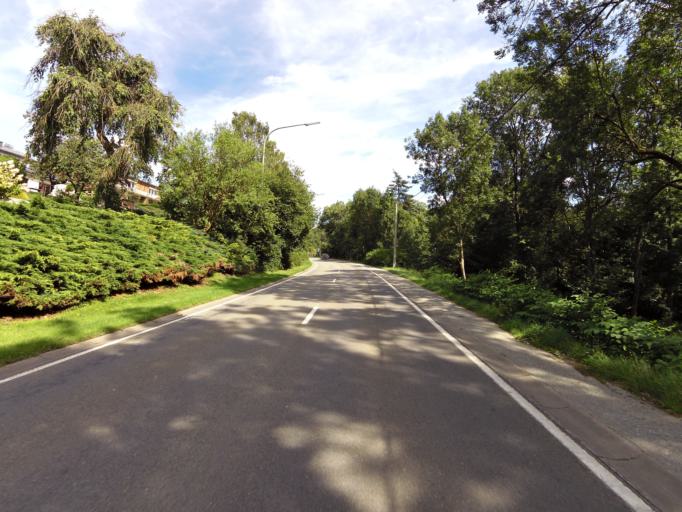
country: BE
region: Wallonia
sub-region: Province du Luxembourg
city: Saint-Hubert
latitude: 50.0291
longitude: 5.3795
